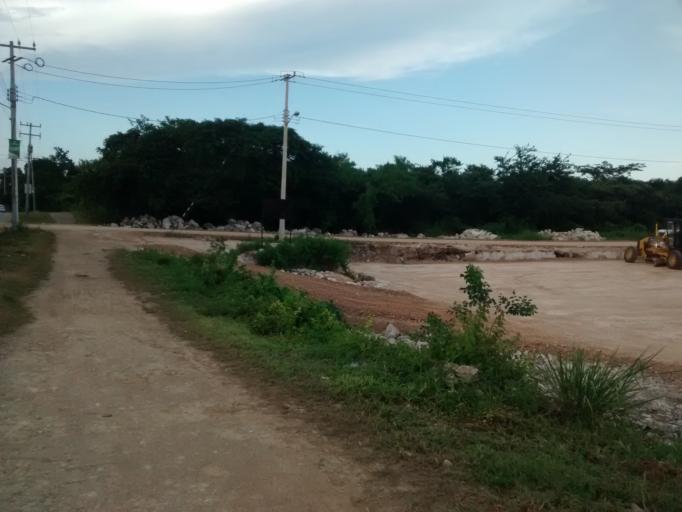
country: MX
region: Yucatan
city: Valladolid
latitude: 20.6868
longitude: -88.1815
